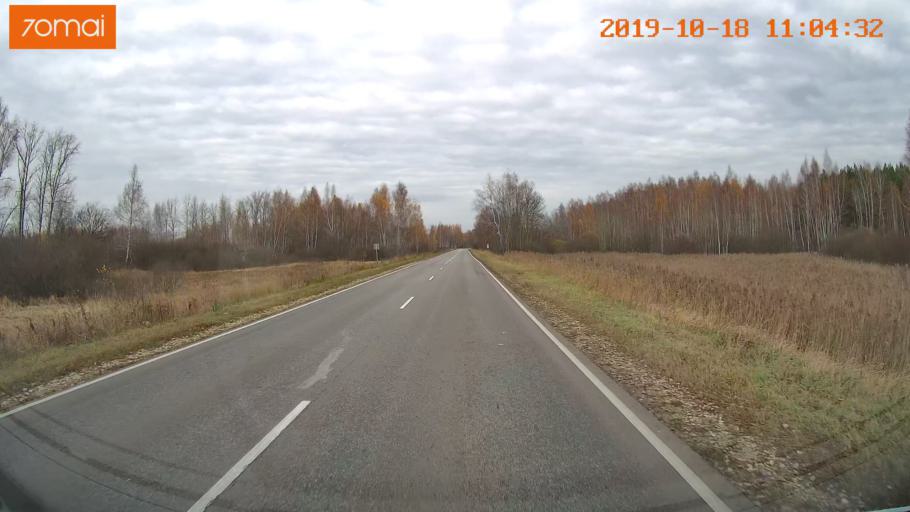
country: RU
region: Tula
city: Yepifan'
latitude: 53.8946
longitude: 38.5461
